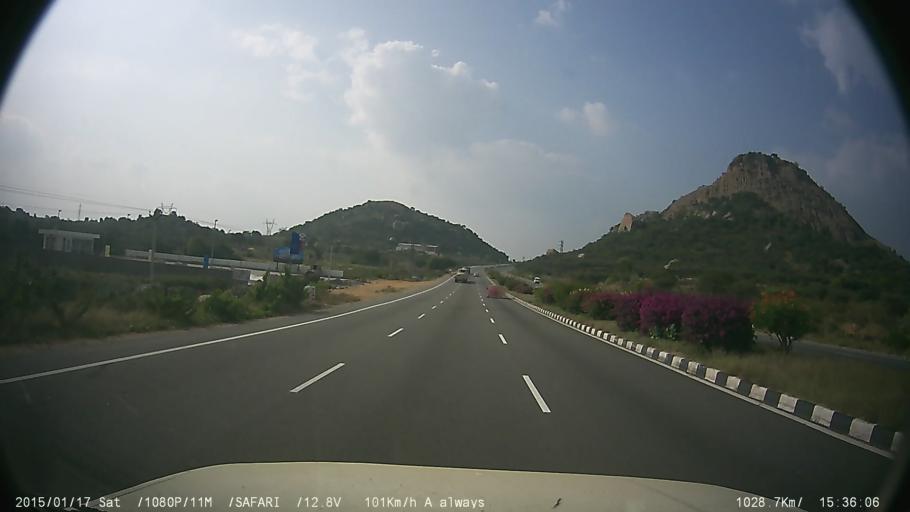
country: IN
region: Tamil Nadu
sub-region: Krishnagiri
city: Kelamangalam
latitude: 12.6540
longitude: 78.0262
